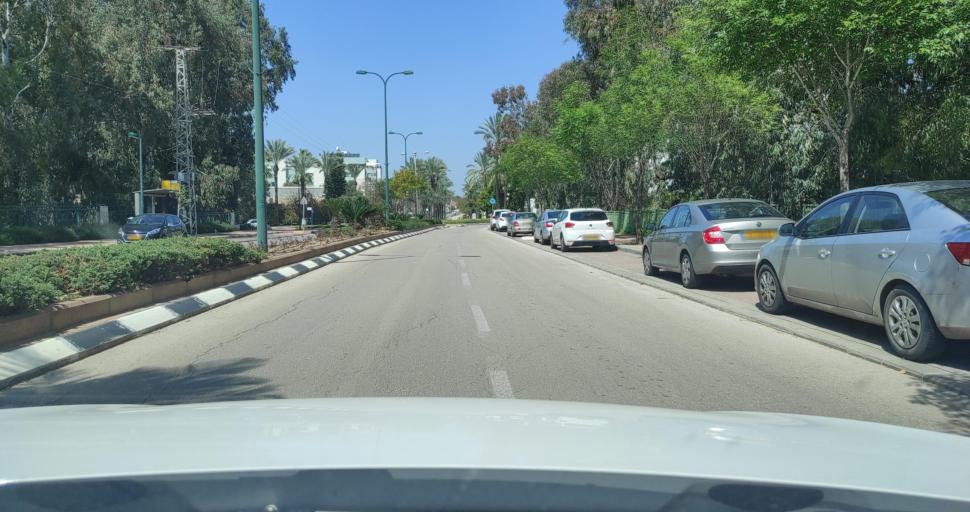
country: IL
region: Central District
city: Nordiyya
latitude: 32.3059
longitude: 34.8807
